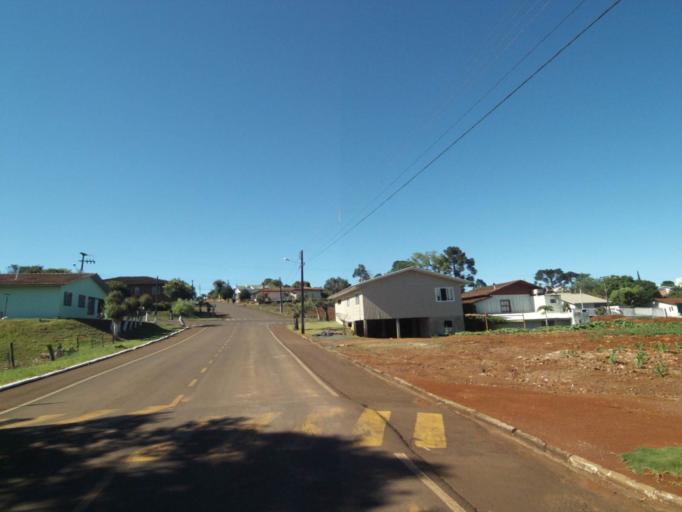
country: BR
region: Parana
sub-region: Pato Branco
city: Pato Branco
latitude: -26.2644
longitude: -52.7766
